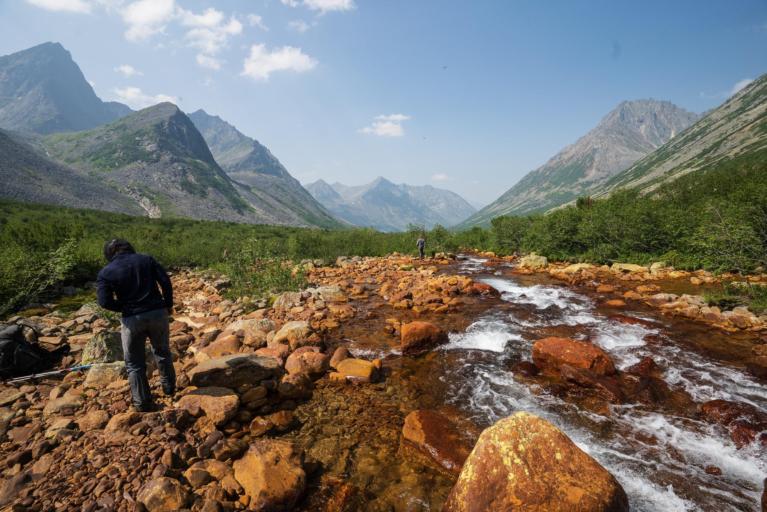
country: RU
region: Transbaikal Territory
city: Kuanda
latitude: 56.8082
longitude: 116.8967
